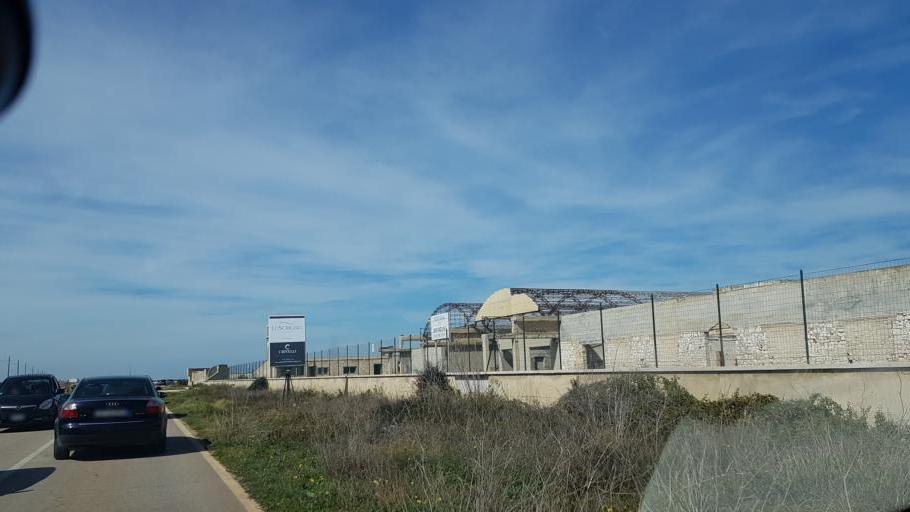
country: IT
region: Apulia
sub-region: Provincia di Brindisi
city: Pezze di Greco
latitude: 40.8599
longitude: 17.4308
